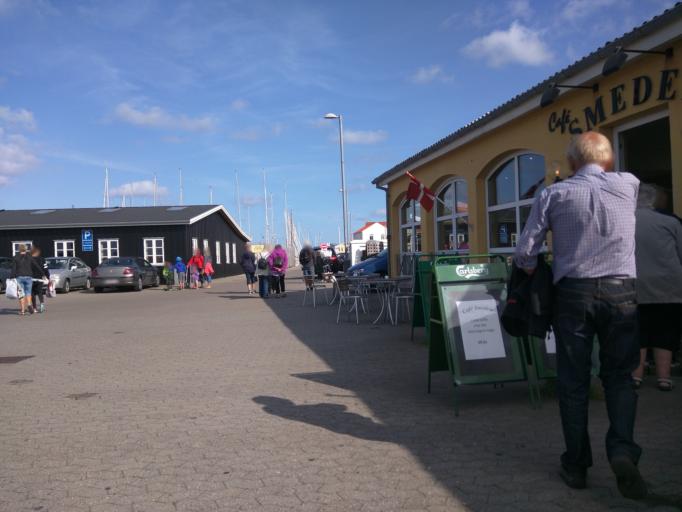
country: DK
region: North Denmark
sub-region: Frederikshavn Kommune
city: Saeby
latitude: 57.3343
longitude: 10.5280
